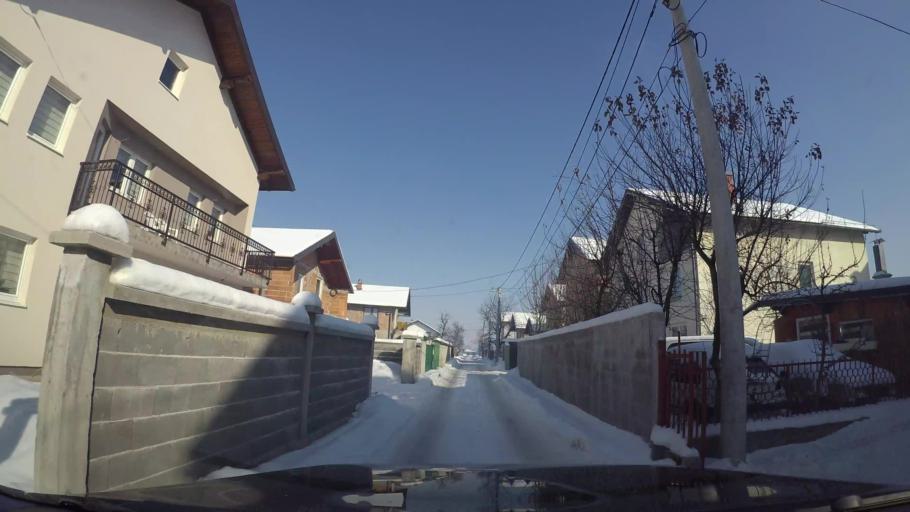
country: BA
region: Federation of Bosnia and Herzegovina
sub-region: Kanton Sarajevo
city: Sarajevo
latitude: 43.8012
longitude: 18.3069
